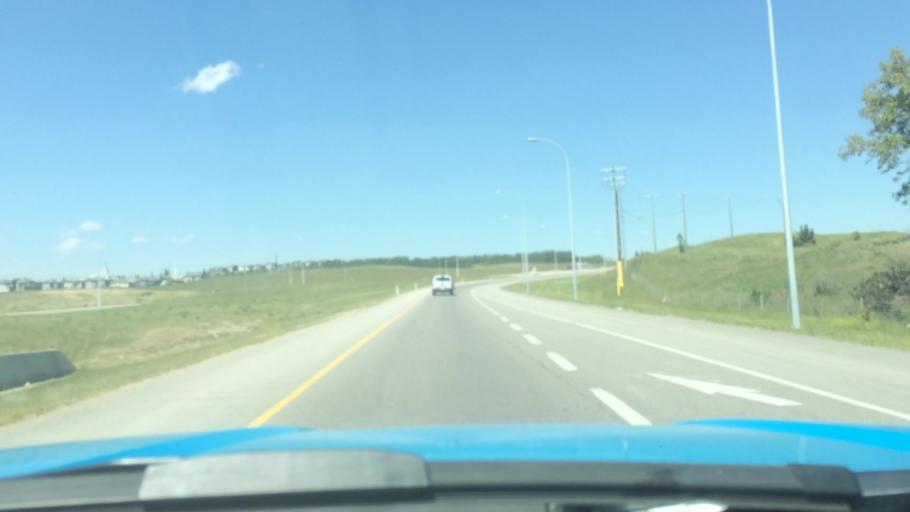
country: CA
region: Alberta
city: Calgary
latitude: 51.1309
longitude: -114.2232
